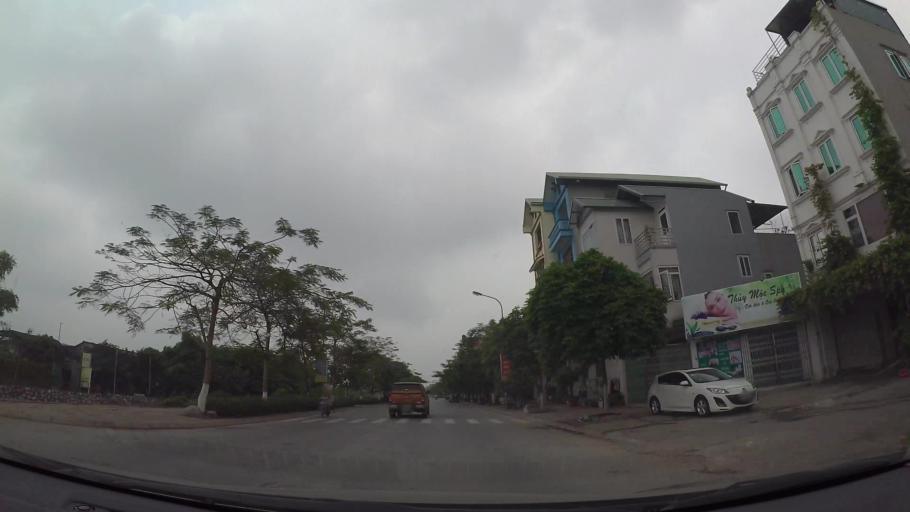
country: VN
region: Ha Noi
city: Trau Quy
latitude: 21.0498
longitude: 105.9220
